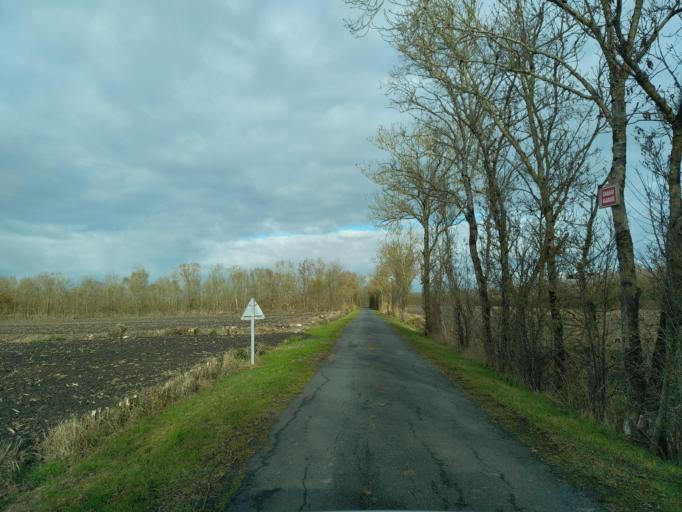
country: FR
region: Pays de la Loire
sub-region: Departement de la Vendee
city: Maillezais
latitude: 46.3266
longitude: -0.7948
